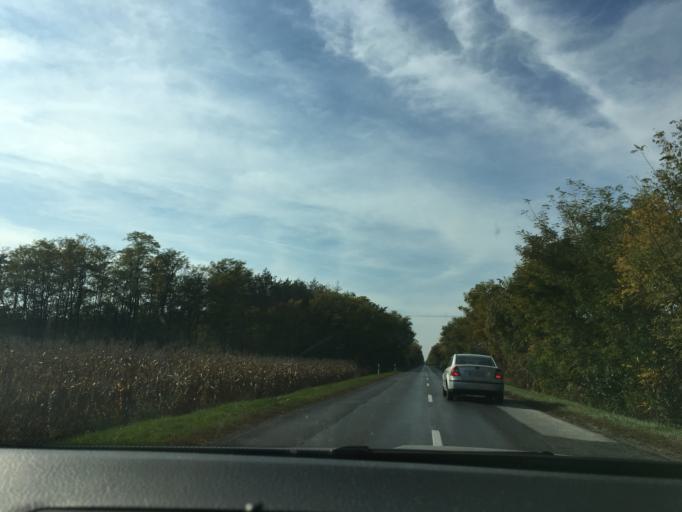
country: HU
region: Hajdu-Bihar
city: Hajdusamson
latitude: 47.5276
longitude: 21.8027
